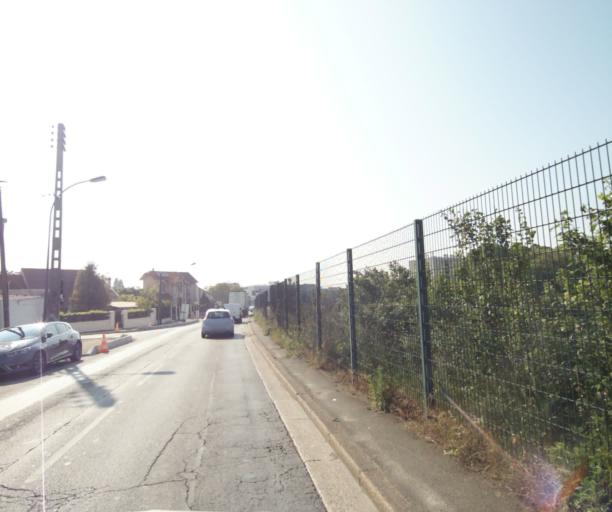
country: FR
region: Ile-de-France
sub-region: Departement du Val-d'Oise
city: Argenteuil
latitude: 48.9553
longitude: 2.2523
